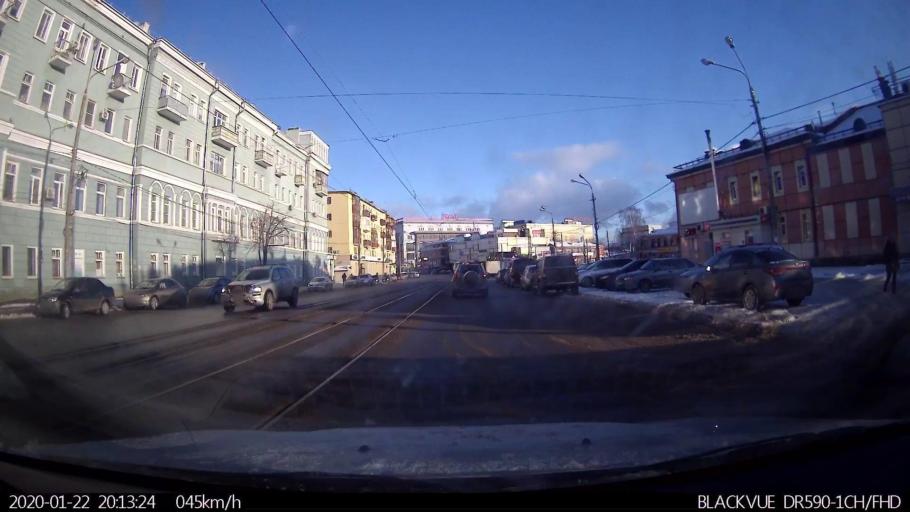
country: RU
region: Nizjnij Novgorod
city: Nizhniy Novgorod
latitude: 56.3178
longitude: 43.9376
